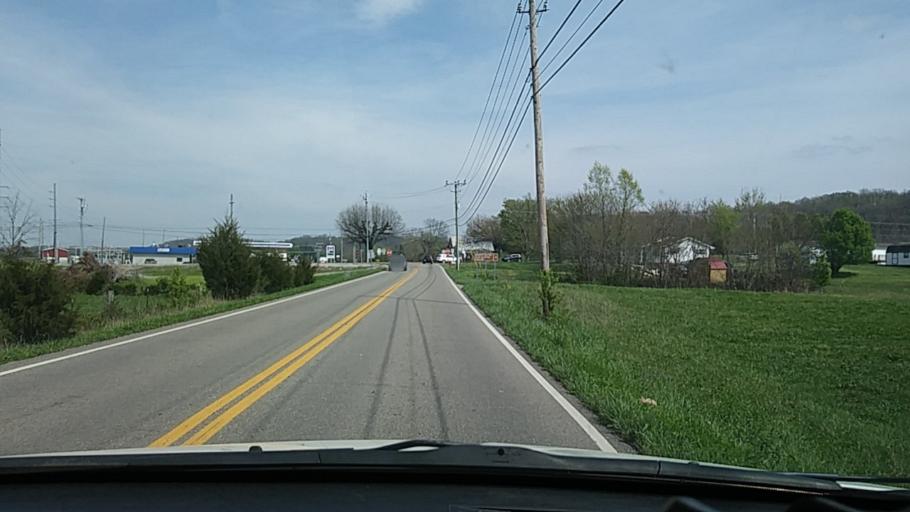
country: US
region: Tennessee
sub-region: Greene County
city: Tusculum
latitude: 36.1058
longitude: -82.7734
